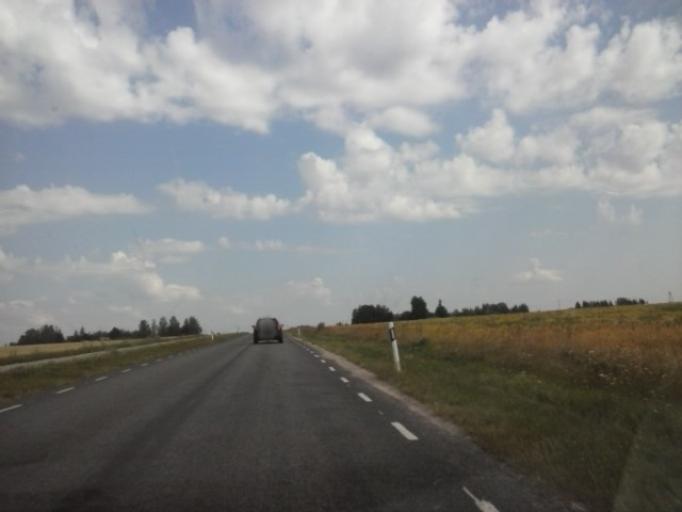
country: EE
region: Jogevamaa
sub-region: Tabivere vald
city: Tabivere
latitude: 58.5119
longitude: 26.6843
